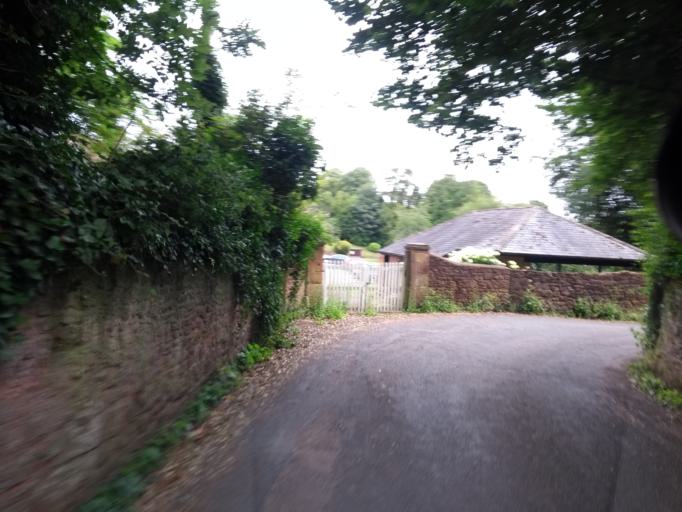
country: GB
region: England
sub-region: Somerset
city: Bishops Lydeard
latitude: 51.0435
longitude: -3.2292
